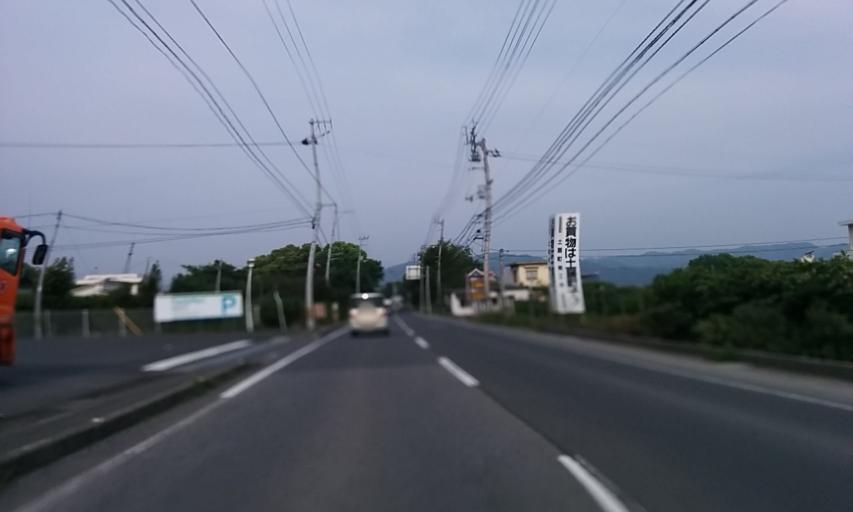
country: JP
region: Ehime
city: Kawanoecho
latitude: 33.9606
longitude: 133.4483
